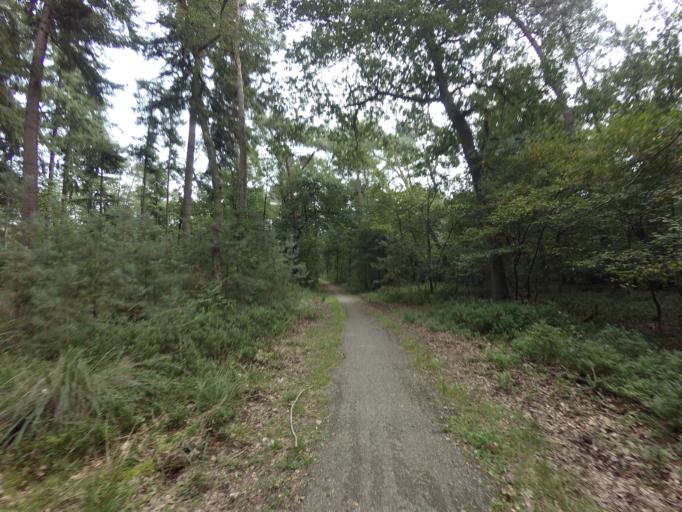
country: NL
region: Gelderland
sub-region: Gemeente Ede
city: Wekerom
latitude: 52.0705
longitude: 5.7085
